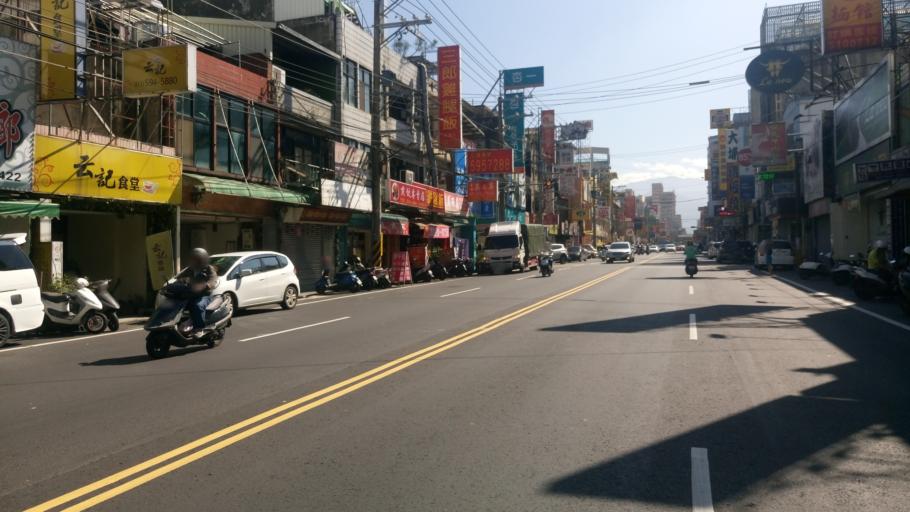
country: TW
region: Taiwan
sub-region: Hsinchu
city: Zhubei
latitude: 24.7451
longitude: 121.0822
